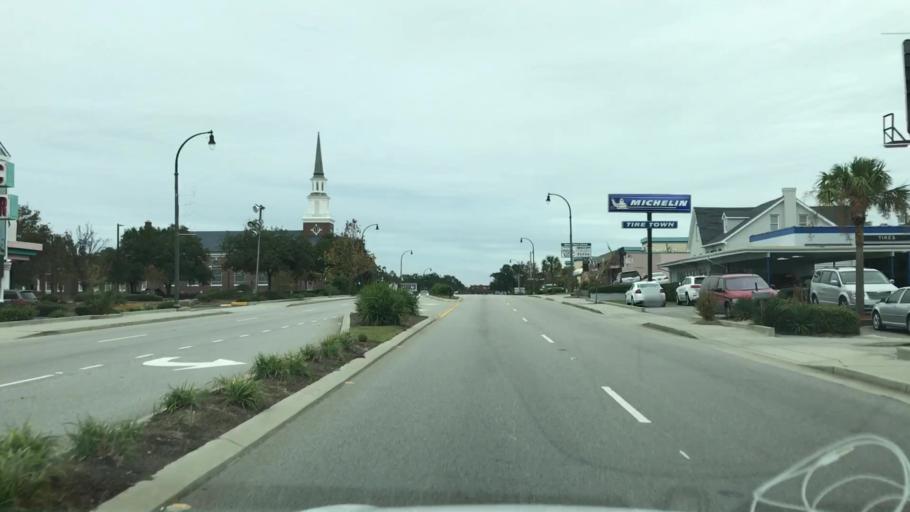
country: US
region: South Carolina
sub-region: Horry County
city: Myrtle Beach
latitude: 33.6878
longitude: -78.8886
